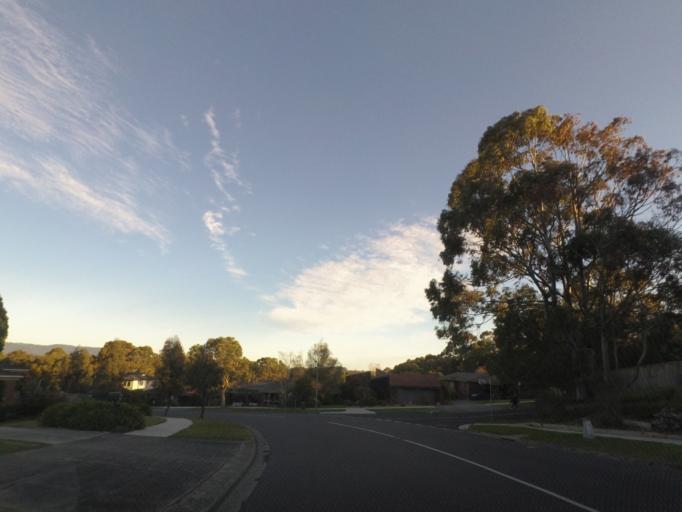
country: AU
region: Victoria
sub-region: Maroondah
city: Warranwood
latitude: -37.7880
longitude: 145.2528
